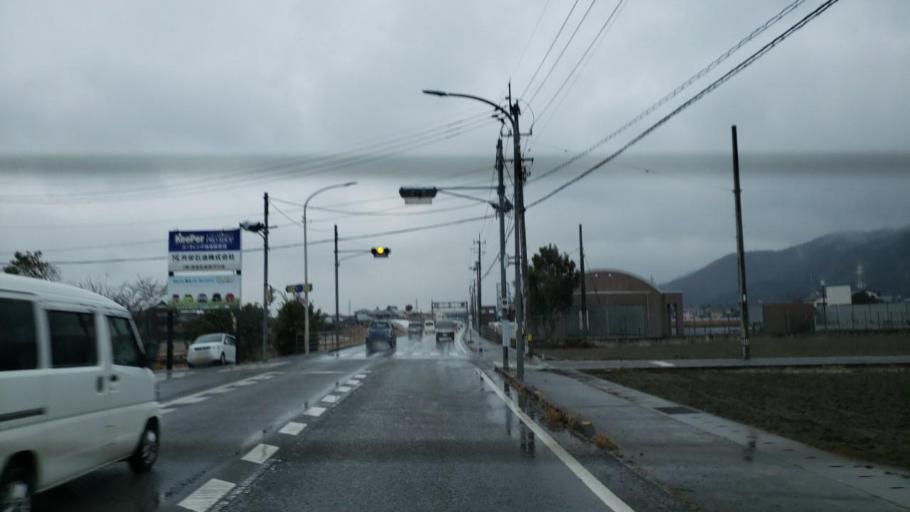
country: JP
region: Tokushima
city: Narutocho-mitsuishi
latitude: 34.1634
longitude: 134.5664
